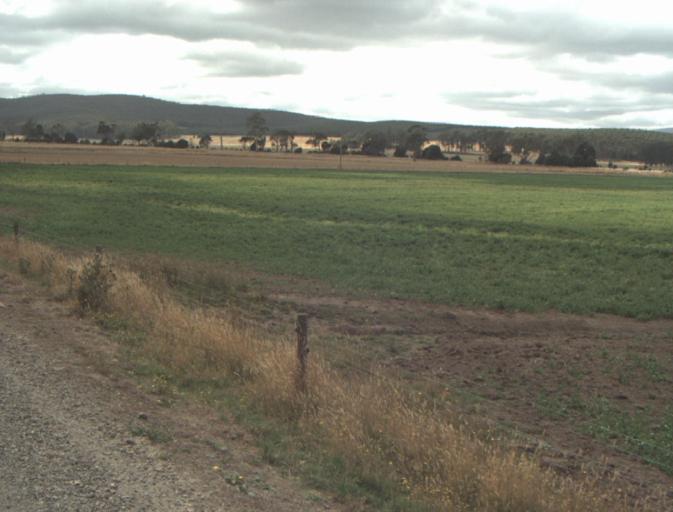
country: AU
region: Tasmania
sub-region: Northern Midlands
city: Evandale
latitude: -41.4804
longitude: 147.4427
